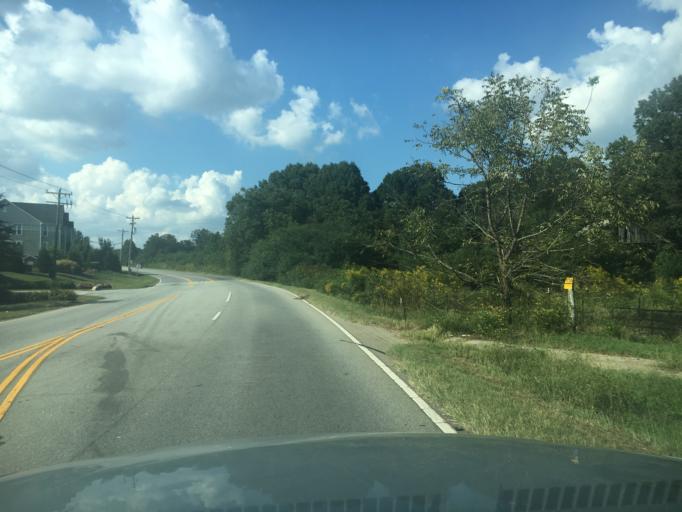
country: US
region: South Carolina
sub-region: Greenville County
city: Simpsonville
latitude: 34.6938
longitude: -82.2530
